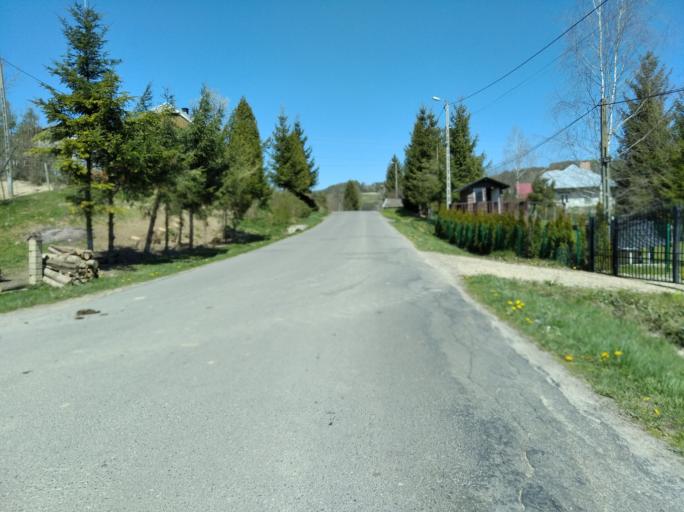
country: PL
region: Subcarpathian Voivodeship
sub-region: Powiat brzozowski
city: Dydnia
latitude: 49.6961
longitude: 22.1514
